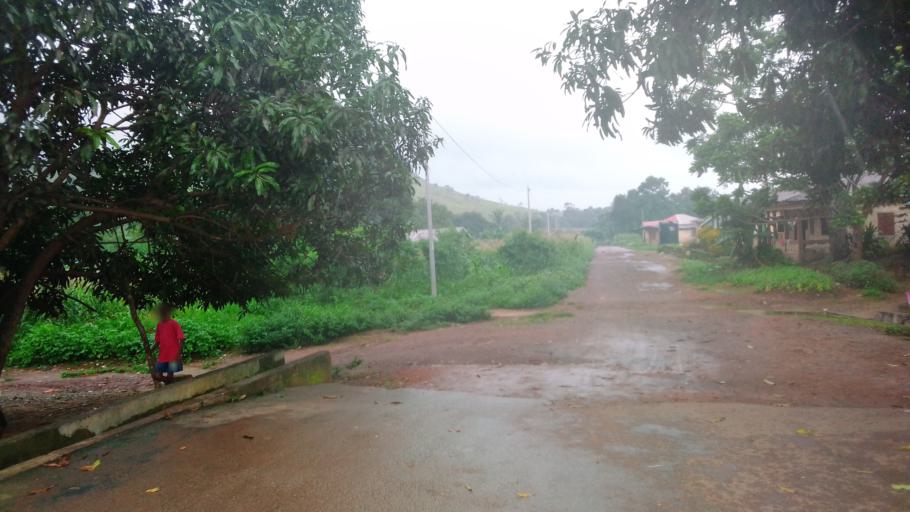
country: SL
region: Northern Province
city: Lunsar
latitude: 8.6830
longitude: -12.5284
